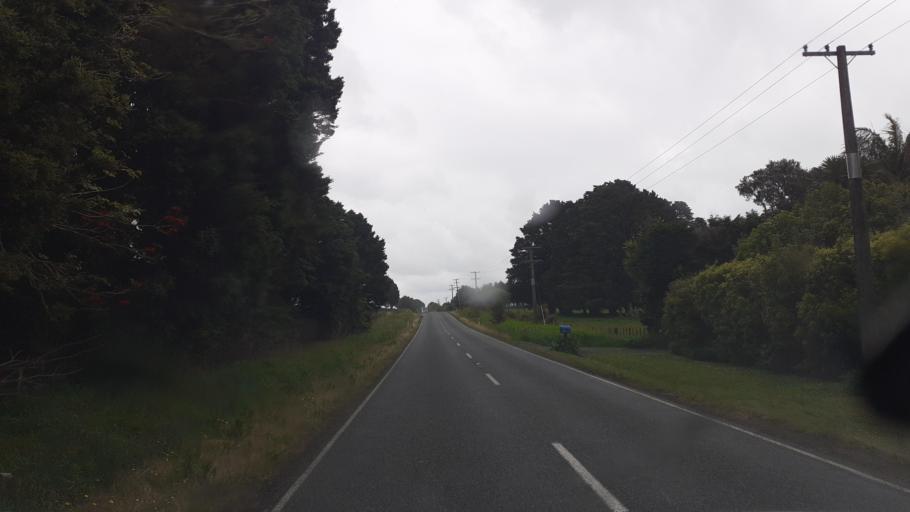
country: NZ
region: Northland
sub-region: Far North District
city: Waimate North
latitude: -35.2916
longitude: 173.8242
